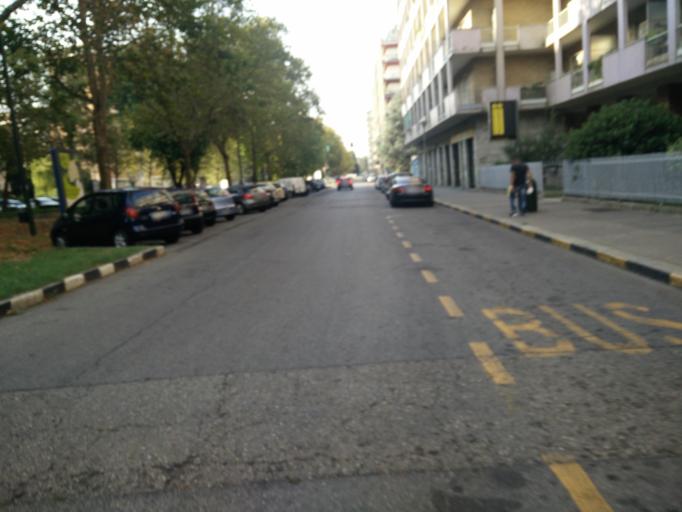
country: IT
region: Piedmont
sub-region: Provincia di Torino
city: Lesna
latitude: 45.0386
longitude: 7.6340
